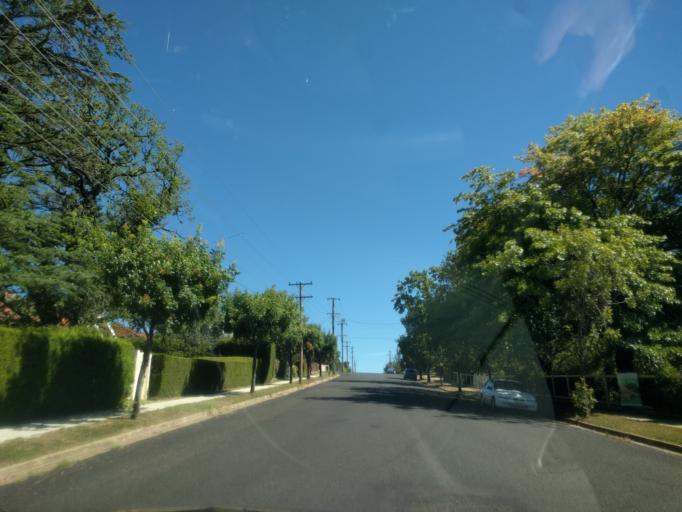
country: AU
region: New South Wales
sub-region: Armidale Dumaresq
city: Armidale
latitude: -30.5218
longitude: 151.6642
